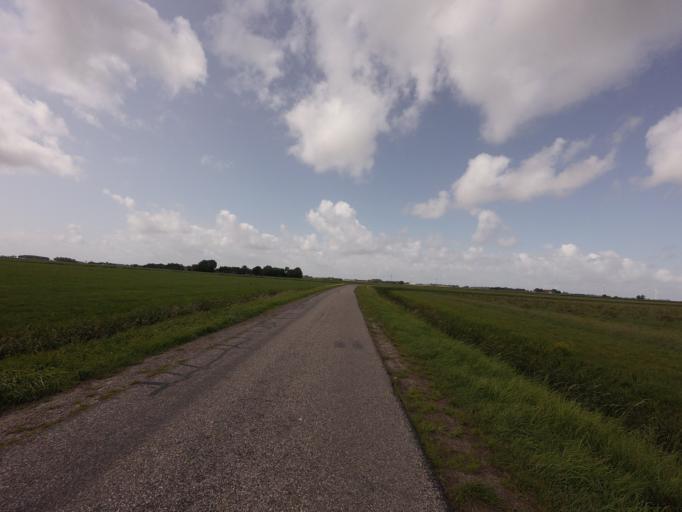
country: NL
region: Friesland
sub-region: Gemeente Franekeradeel
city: Sexbierum
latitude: 53.1654
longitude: 5.4863
